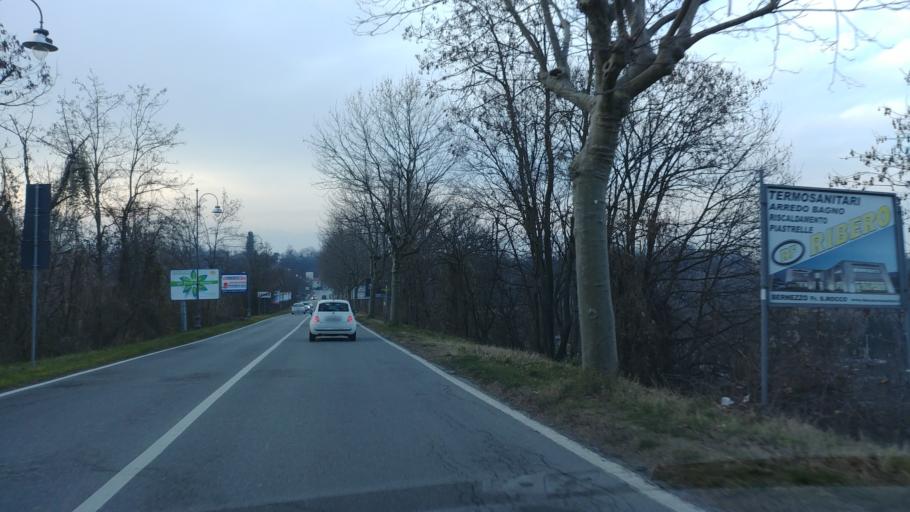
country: IT
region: Piedmont
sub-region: Provincia di Cuneo
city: Cuneo
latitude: 44.3964
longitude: 7.5483
